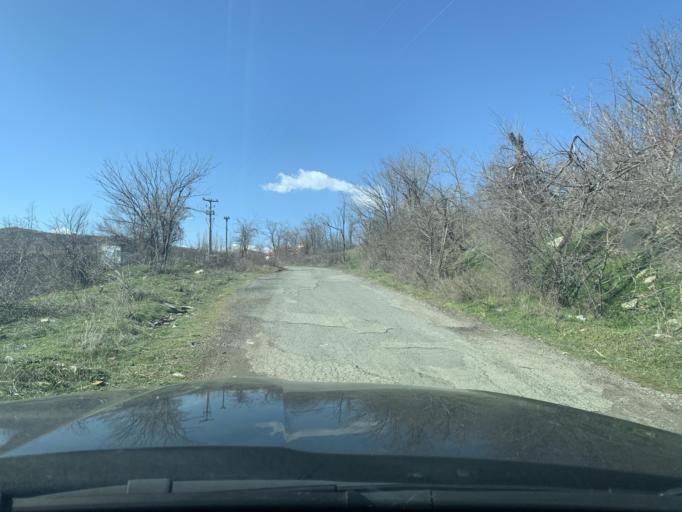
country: MK
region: Demir Kapija
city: Demir Kapija
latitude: 41.4095
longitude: 22.2306
